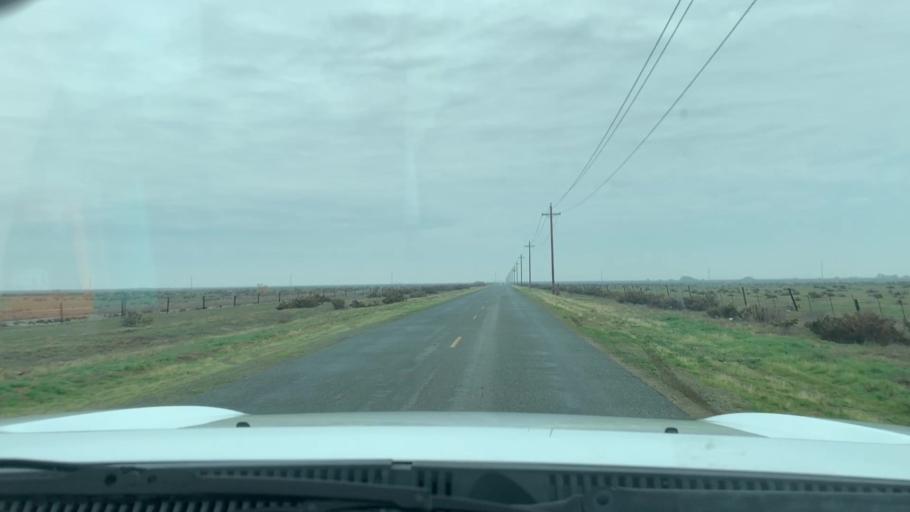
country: US
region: California
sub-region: Tulare County
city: Alpaugh
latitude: 35.7610
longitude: -119.4714
